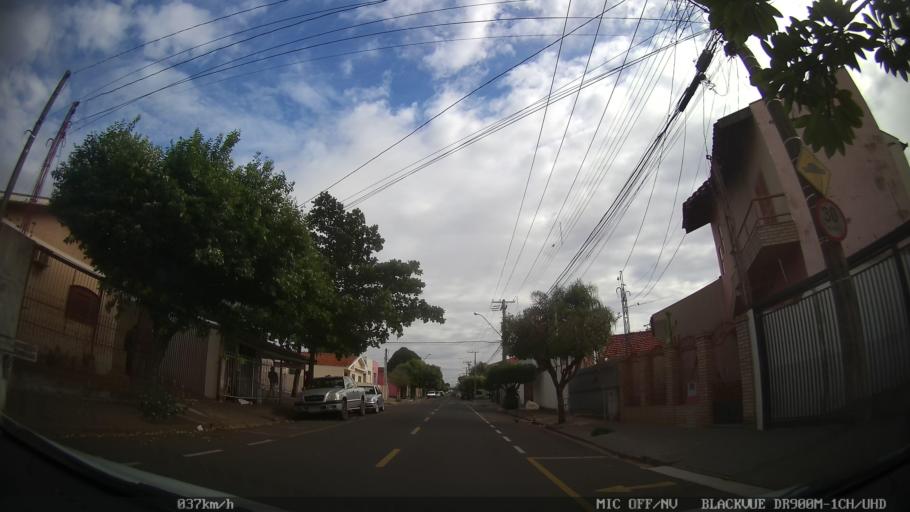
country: BR
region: Sao Paulo
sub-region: Sao Jose Do Rio Preto
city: Sao Jose do Rio Preto
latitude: -20.8234
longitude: -49.3505
